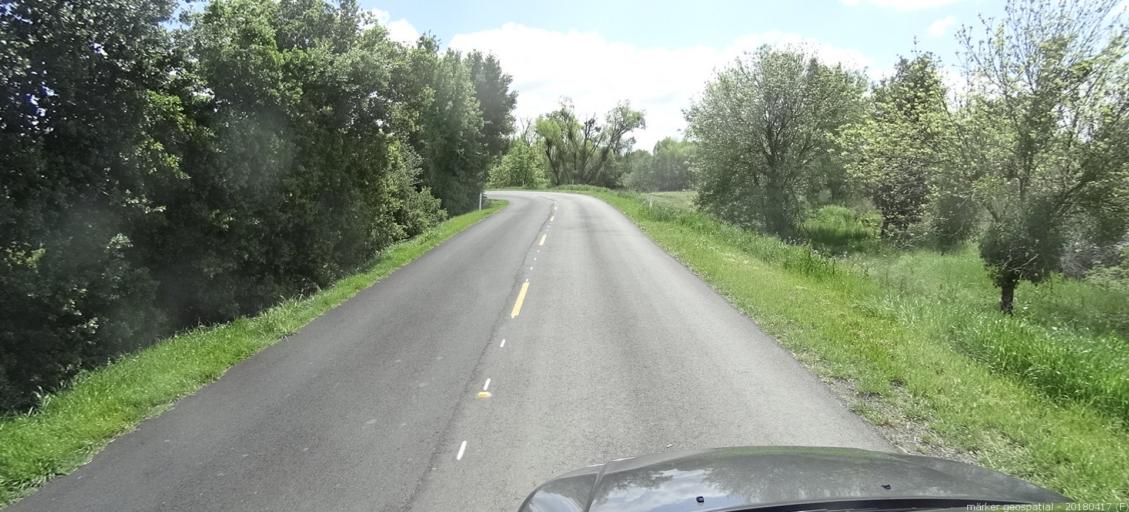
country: US
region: California
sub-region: Sacramento County
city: Walnut Grove
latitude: 38.2270
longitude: -121.5283
